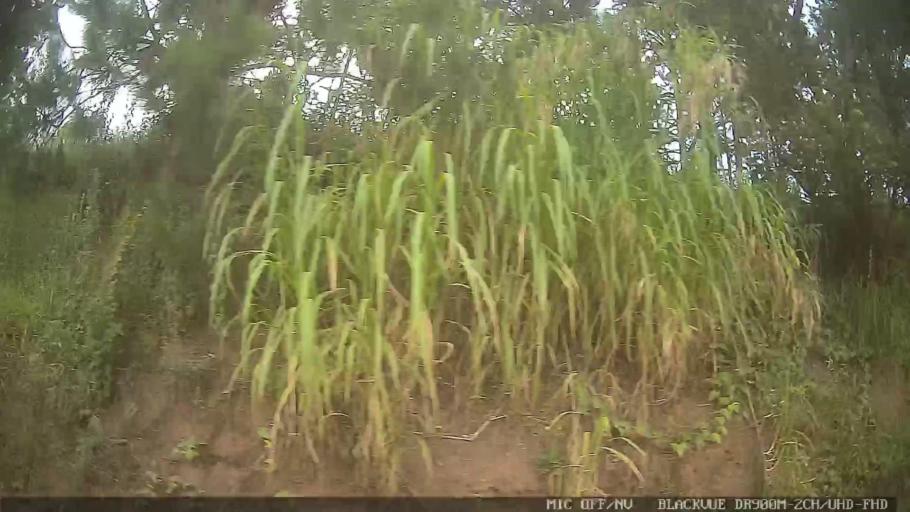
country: BR
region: Sao Paulo
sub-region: Atibaia
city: Atibaia
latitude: -23.0364
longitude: -46.5299
